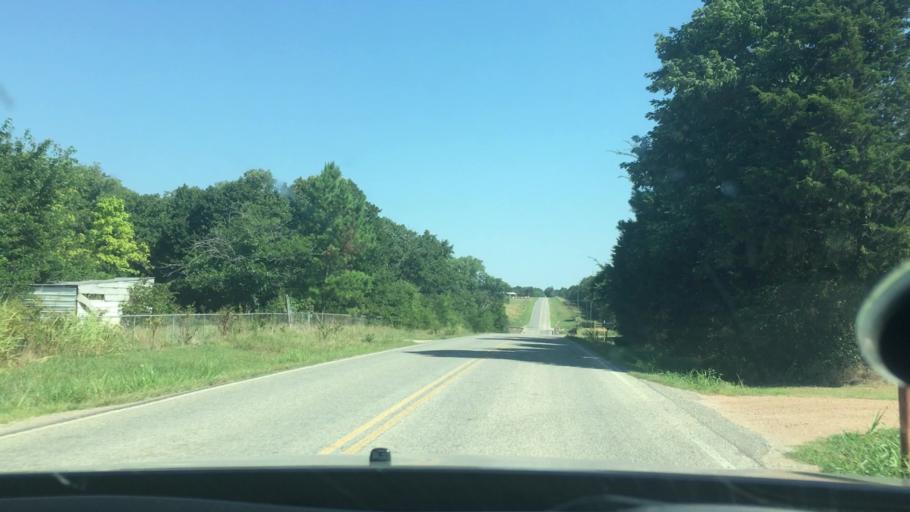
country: US
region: Oklahoma
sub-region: Johnston County
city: Tishomingo
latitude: 34.2715
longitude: -96.6186
